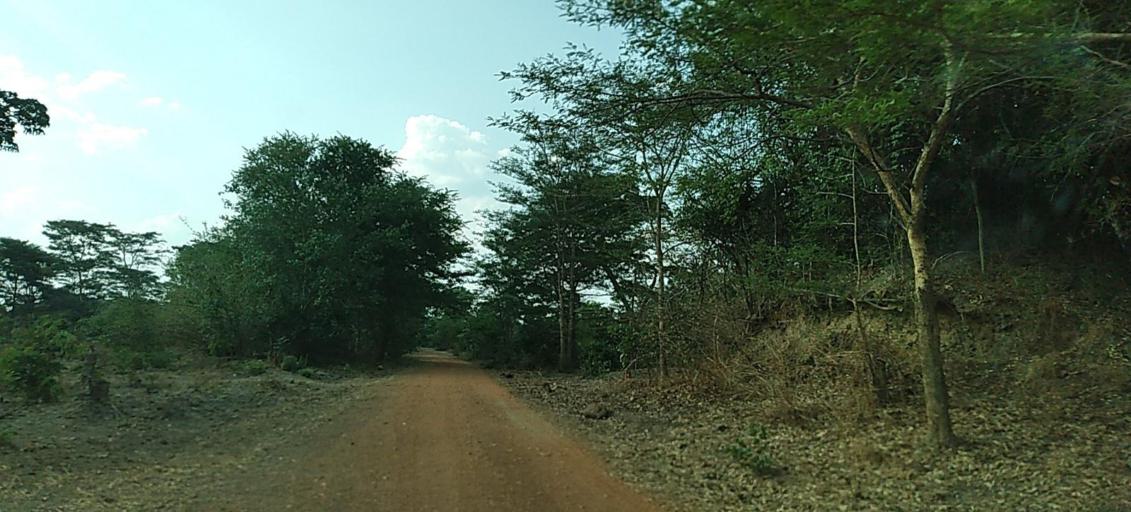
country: ZM
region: Copperbelt
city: Mpongwe
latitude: -13.4710
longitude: 28.0709
